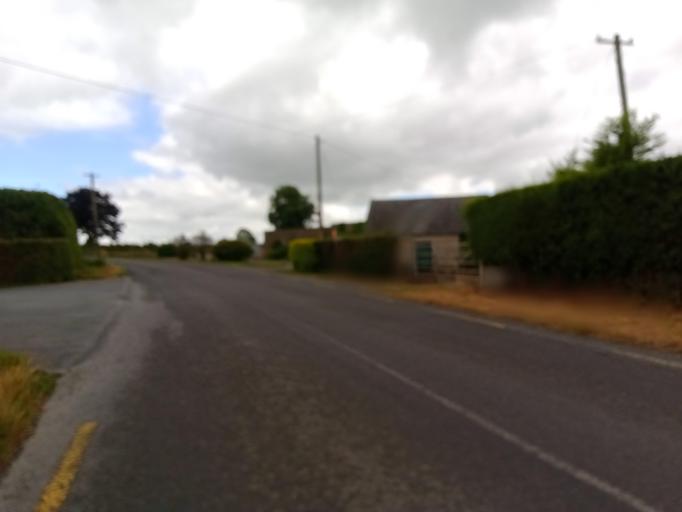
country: IE
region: Leinster
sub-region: Kilkenny
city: Callan
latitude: 52.5734
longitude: -7.4041
